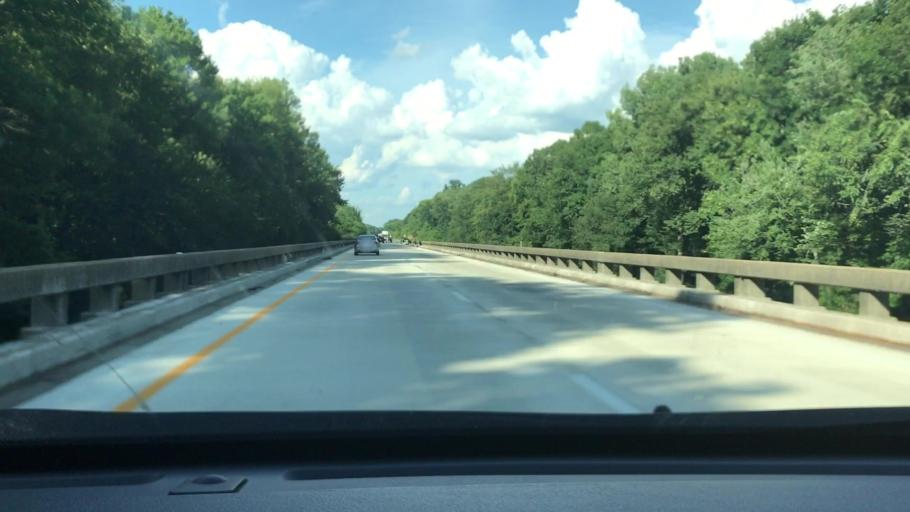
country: US
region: South Carolina
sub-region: Florence County
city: Florence
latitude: 34.3002
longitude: -79.6321
